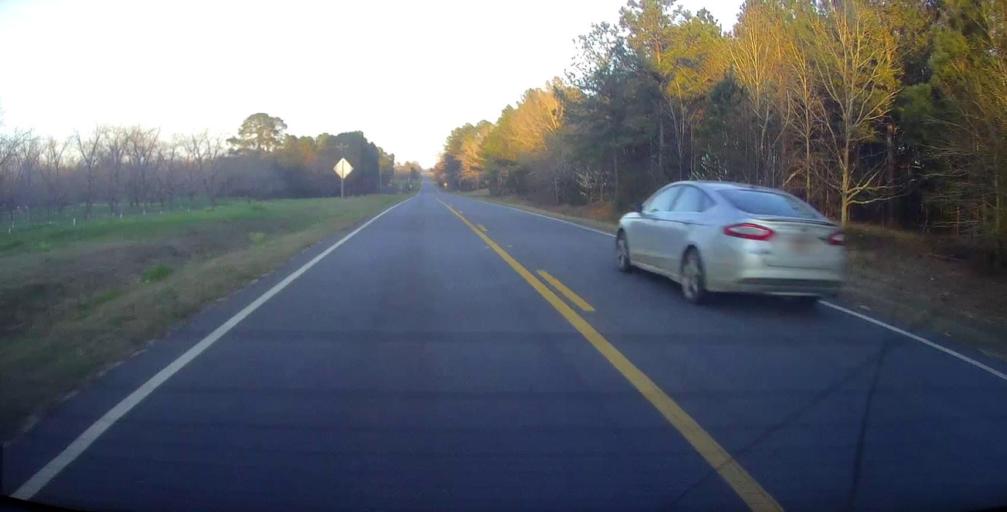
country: US
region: Georgia
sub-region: Dodge County
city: Chester
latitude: 32.3502
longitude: -83.0312
